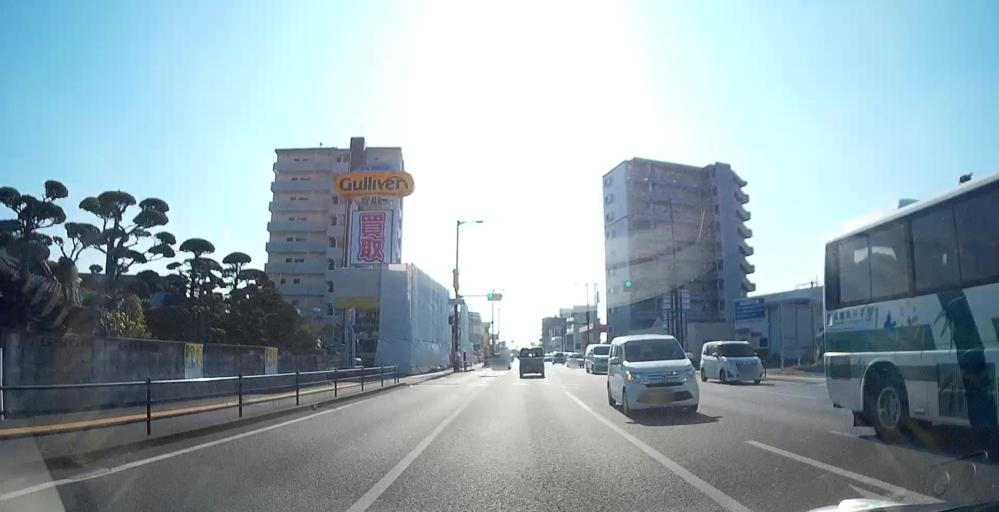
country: JP
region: Kumamoto
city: Kumamoto
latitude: 32.7707
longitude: 130.6938
